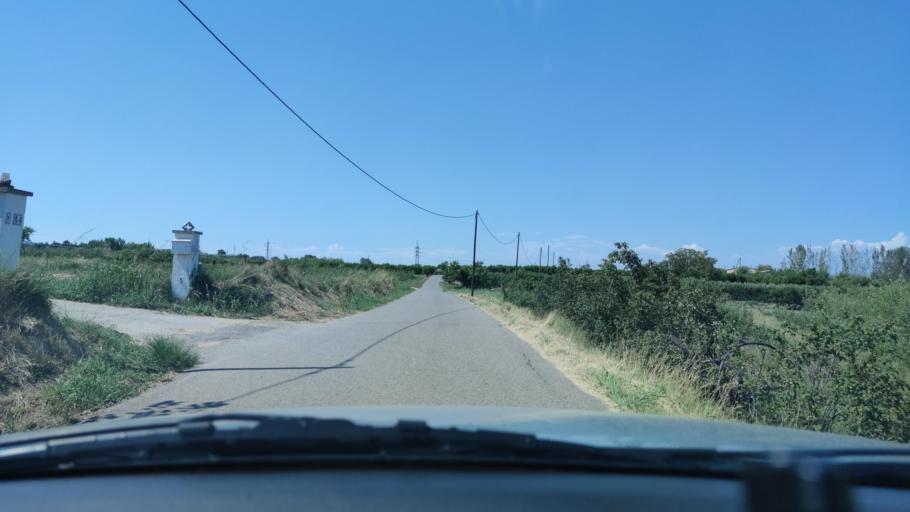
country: ES
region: Catalonia
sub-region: Provincia de Lleida
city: Torrefarrera
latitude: 41.6677
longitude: 0.6194
